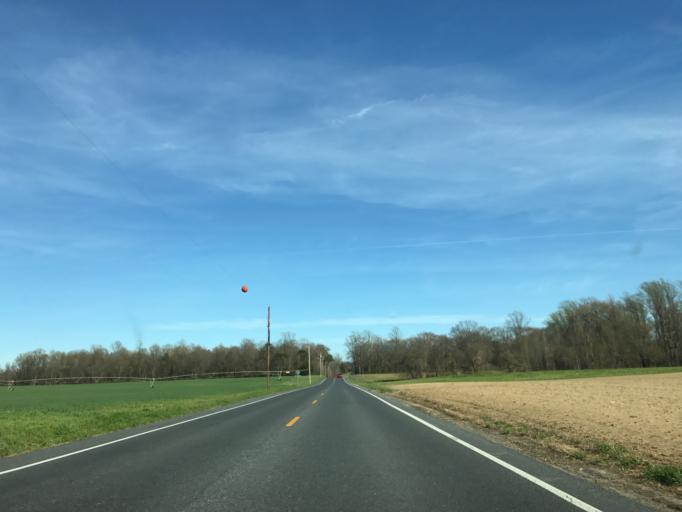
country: US
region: Maryland
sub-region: Caroline County
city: Greensboro
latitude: 39.0325
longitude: -75.7657
